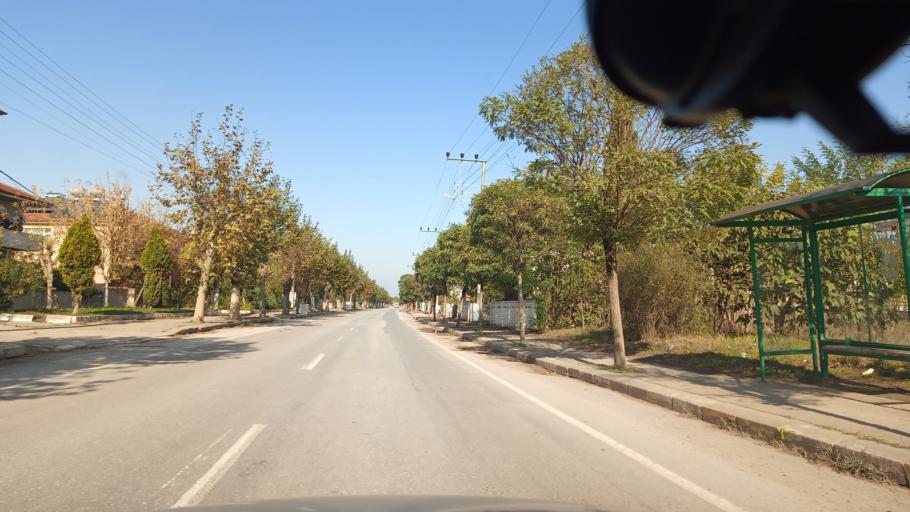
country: TR
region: Sakarya
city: Sogutlu
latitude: 40.8840
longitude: 30.4640
